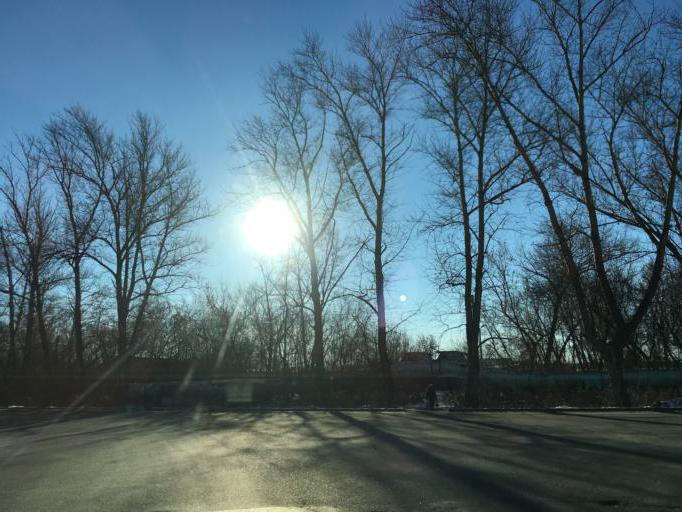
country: RU
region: Tula
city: Tula
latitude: 54.1745
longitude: 37.7045
